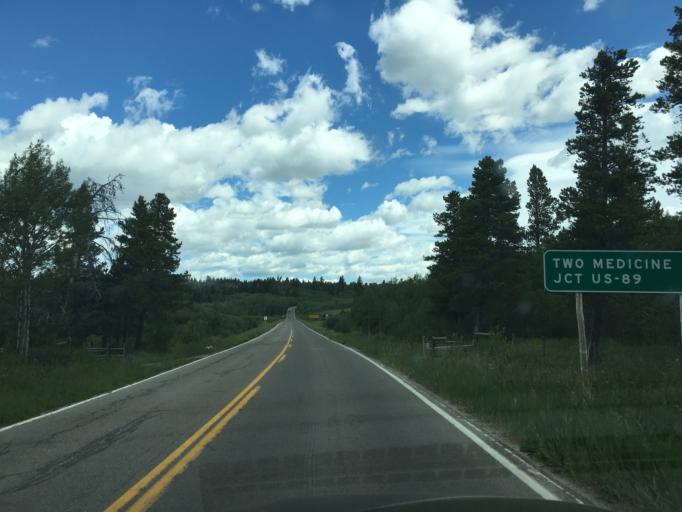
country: US
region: Montana
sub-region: Glacier County
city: South Browning
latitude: 48.4520
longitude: -113.2254
